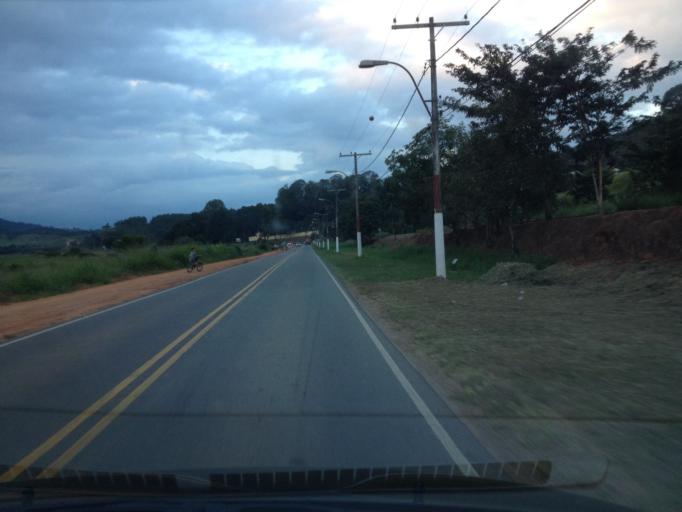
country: BR
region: Minas Gerais
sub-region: Sao Lourenco
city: Sao Lourenco
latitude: -22.0972
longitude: -45.0488
